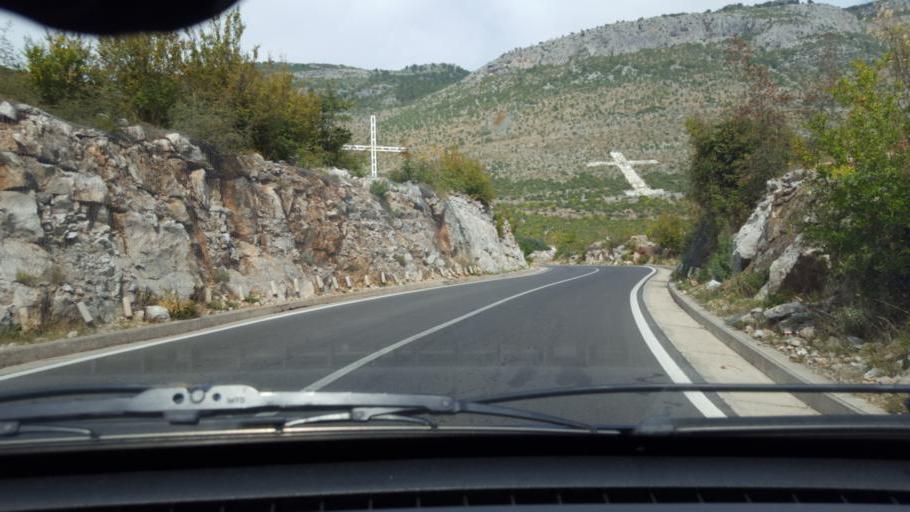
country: AL
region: Shkoder
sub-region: Rrethi i Malesia e Madhe
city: Hot
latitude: 42.3709
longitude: 19.4492
